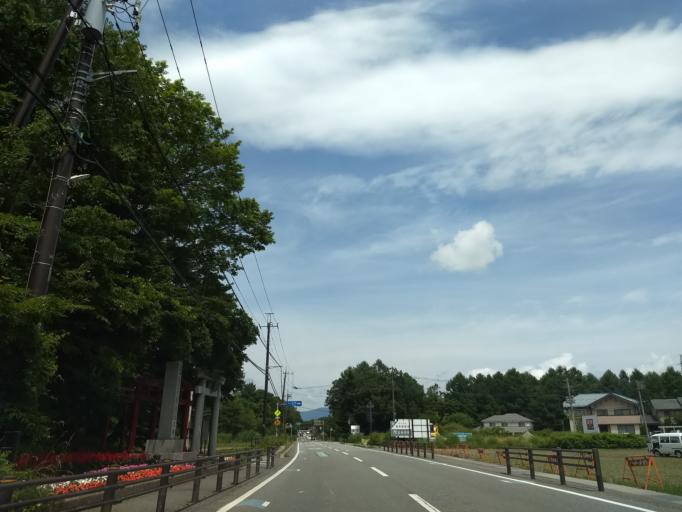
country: JP
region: Shizuoka
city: Gotemba
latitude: 35.4323
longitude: 138.8432
